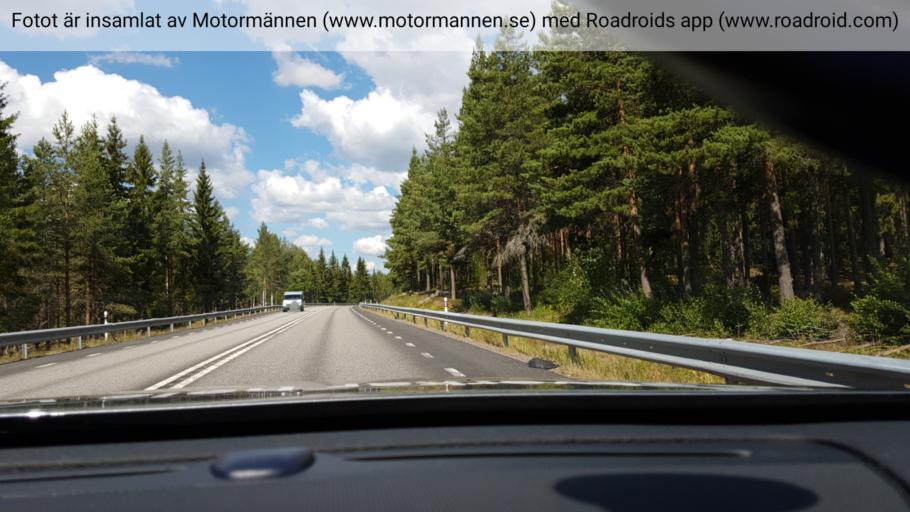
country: SE
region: Dalarna
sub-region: Faluns Kommun
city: Grycksbo
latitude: 60.7023
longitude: 15.4726
